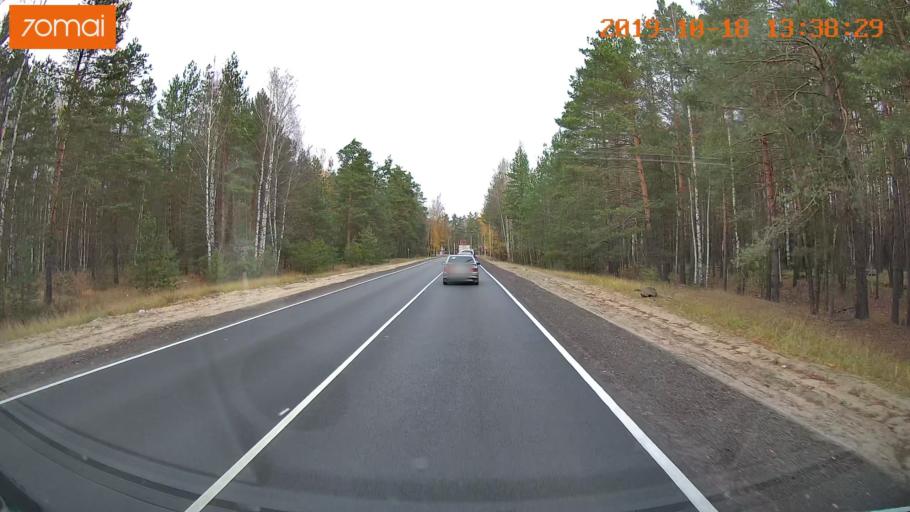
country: RU
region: Rjazan
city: Solotcha
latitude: 54.8905
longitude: 40.0028
